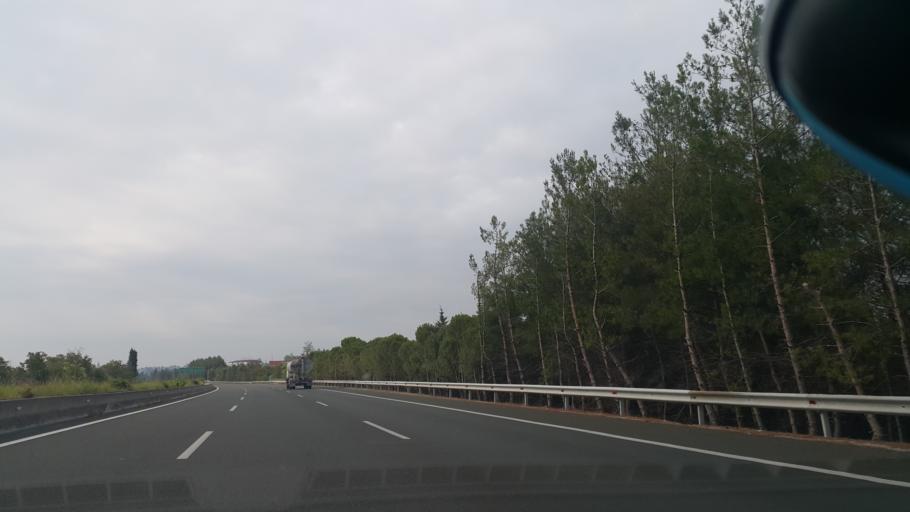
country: GR
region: Central Macedonia
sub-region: Nomos Pierias
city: Aiginio
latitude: 40.4746
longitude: 22.5712
